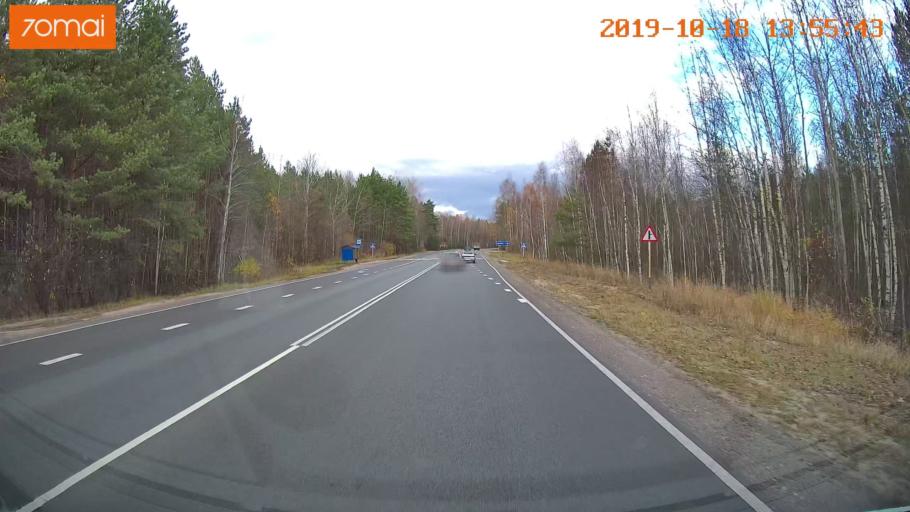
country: RU
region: Rjazan
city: Spas-Klepiki
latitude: 55.0554
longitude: 40.0246
